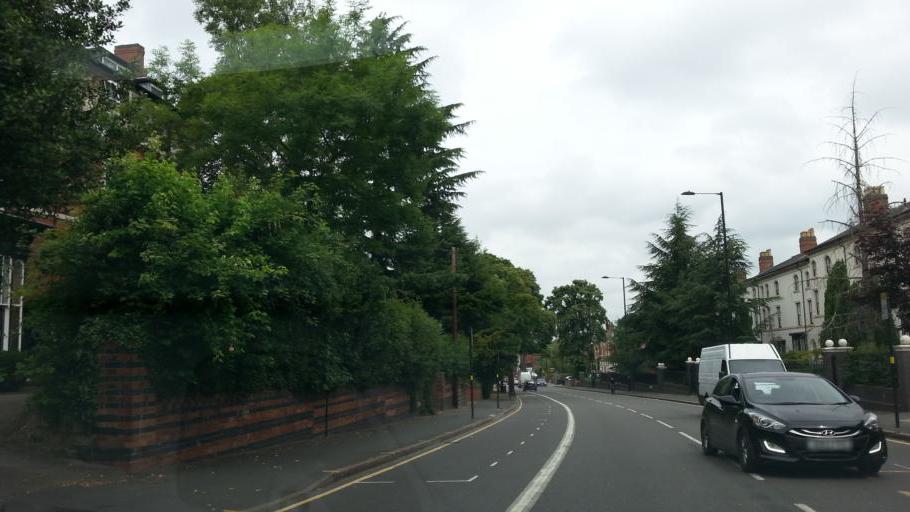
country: GB
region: England
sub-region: City and Borough of Birmingham
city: Birmingham
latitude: 52.4518
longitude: -1.8879
